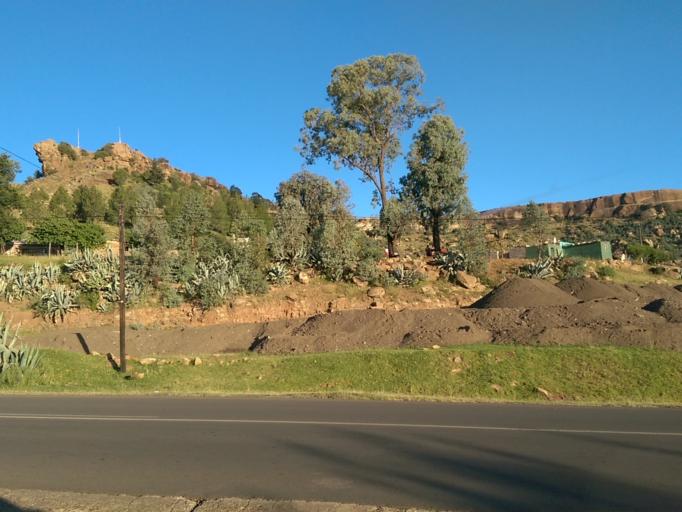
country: LS
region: Maseru
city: Maseru
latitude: -29.3473
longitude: 27.6630
